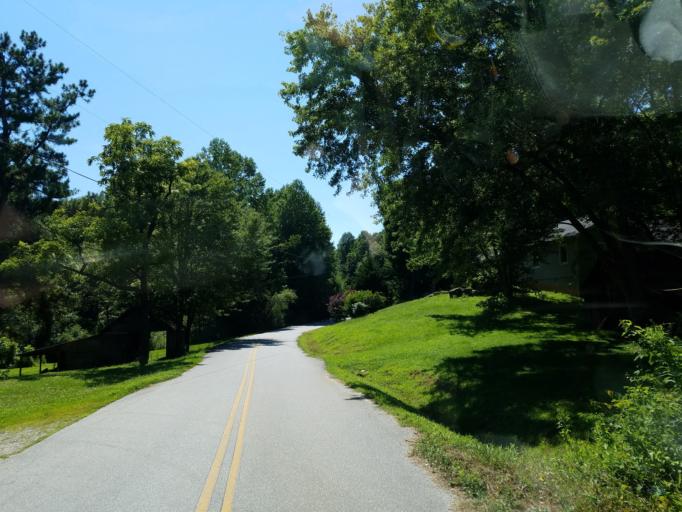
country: US
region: Georgia
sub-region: Lumpkin County
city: Dahlonega
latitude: 34.4146
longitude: -83.9946
